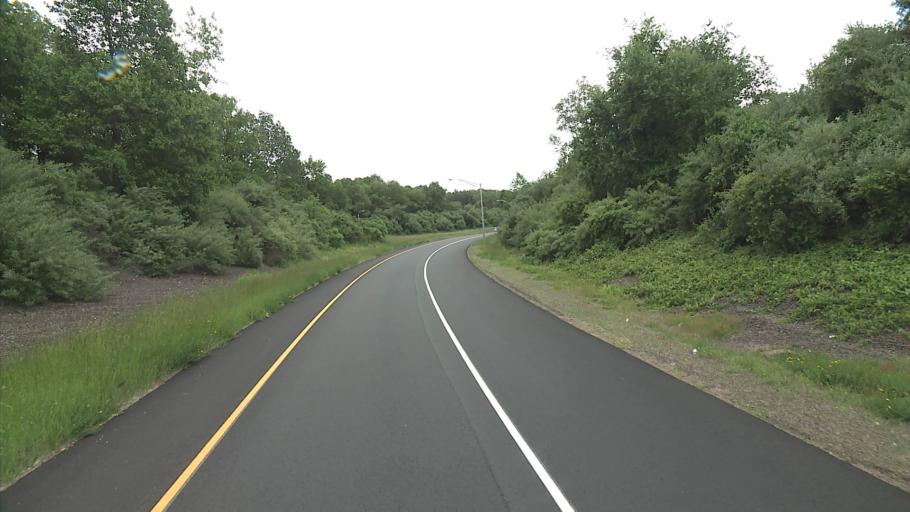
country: US
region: Connecticut
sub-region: Middlesex County
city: Cromwell
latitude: 41.6217
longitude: -72.6871
